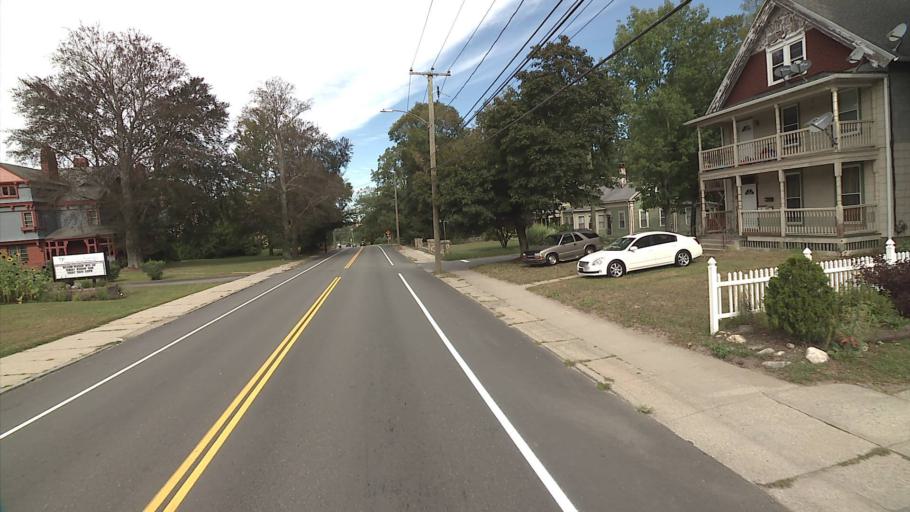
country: US
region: Connecticut
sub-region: Windham County
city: Willimantic
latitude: 41.7078
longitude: -72.2029
